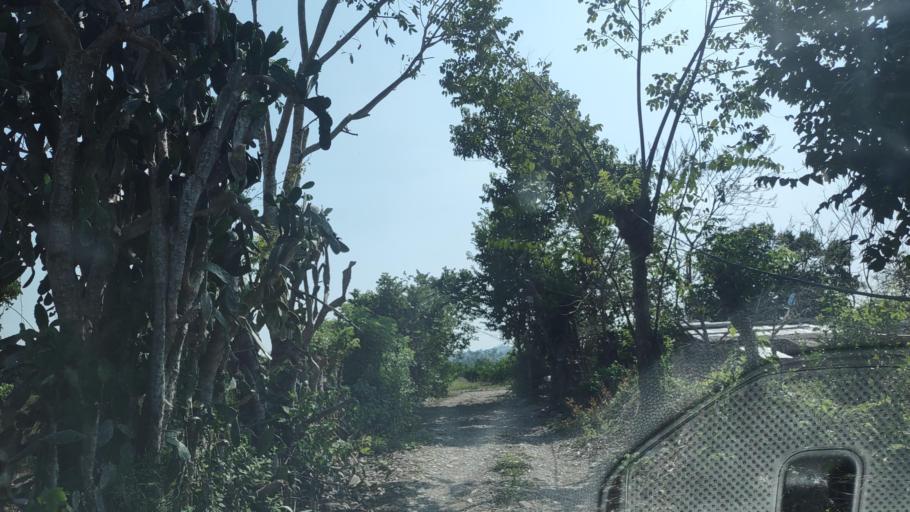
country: MX
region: Puebla
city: Espinal
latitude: 20.2607
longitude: -97.3116
